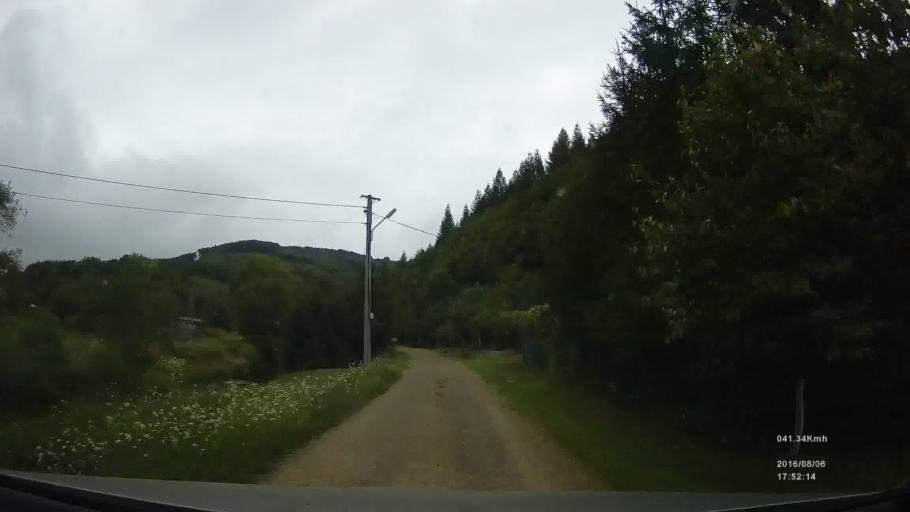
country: SK
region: Presovsky
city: Svidnik
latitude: 49.4043
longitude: 21.5675
